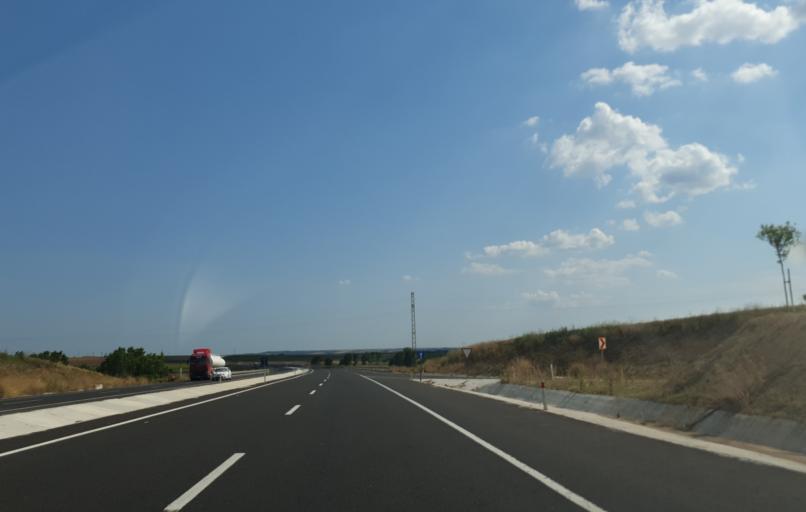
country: TR
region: Tekirdag
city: Muratli
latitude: 41.2243
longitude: 27.5319
